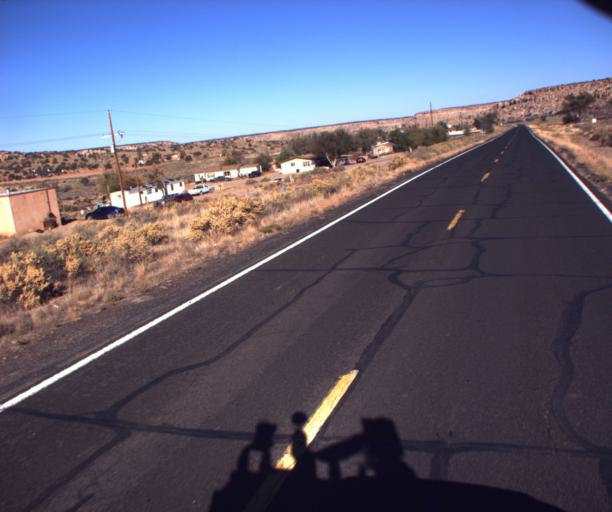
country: US
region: Arizona
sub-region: Navajo County
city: First Mesa
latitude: 35.8208
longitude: -110.2180
